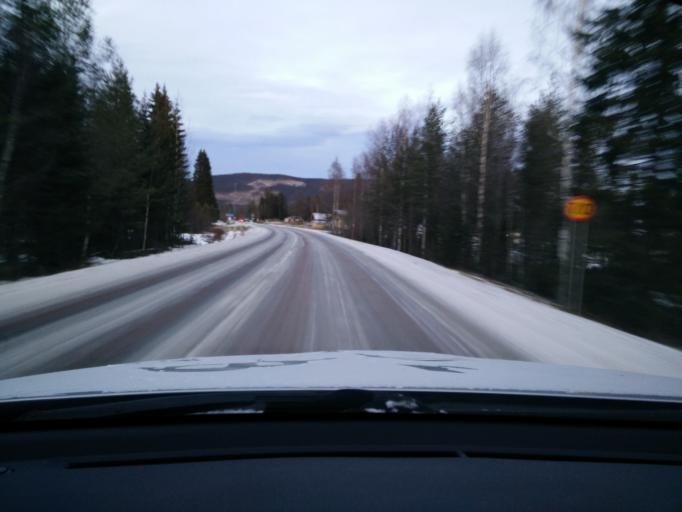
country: SE
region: Jaemtland
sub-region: Bergs Kommun
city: Hoverberg
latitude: 62.4774
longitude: 14.2287
